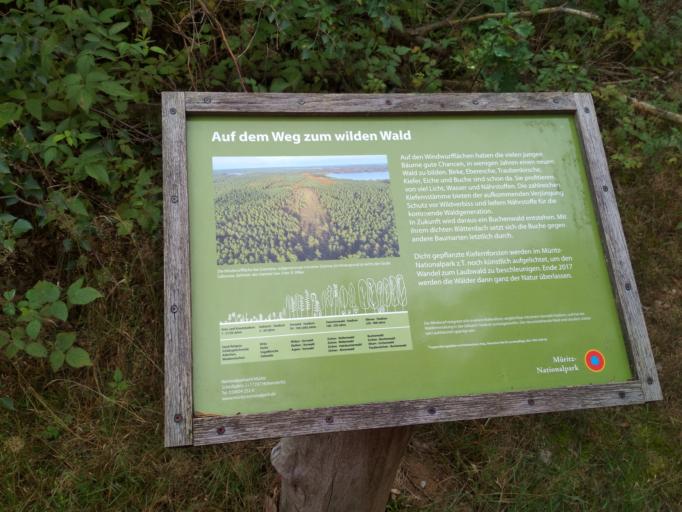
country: DE
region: Mecklenburg-Vorpommern
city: Wesenberg
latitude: 53.3141
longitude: 12.9349
